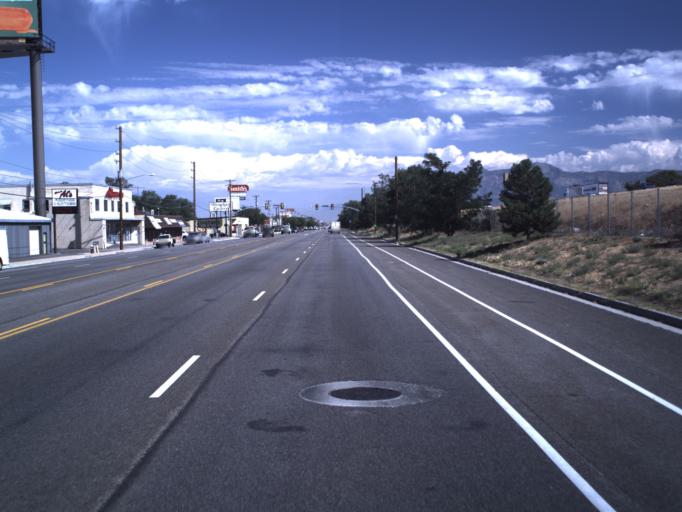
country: US
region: Utah
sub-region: Davis County
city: Sunset
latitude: 41.1452
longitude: -112.0260
